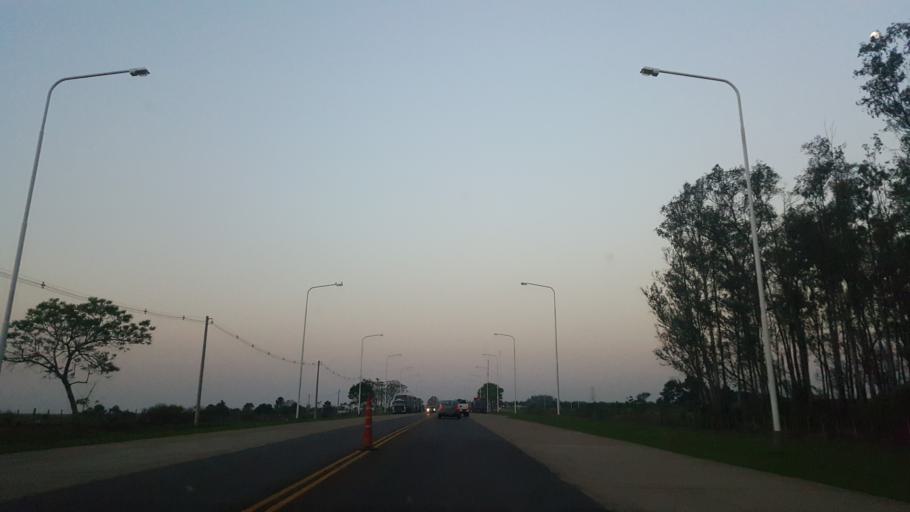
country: PY
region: Itapua
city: San Juan del Parana
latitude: -27.4536
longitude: -56.0480
